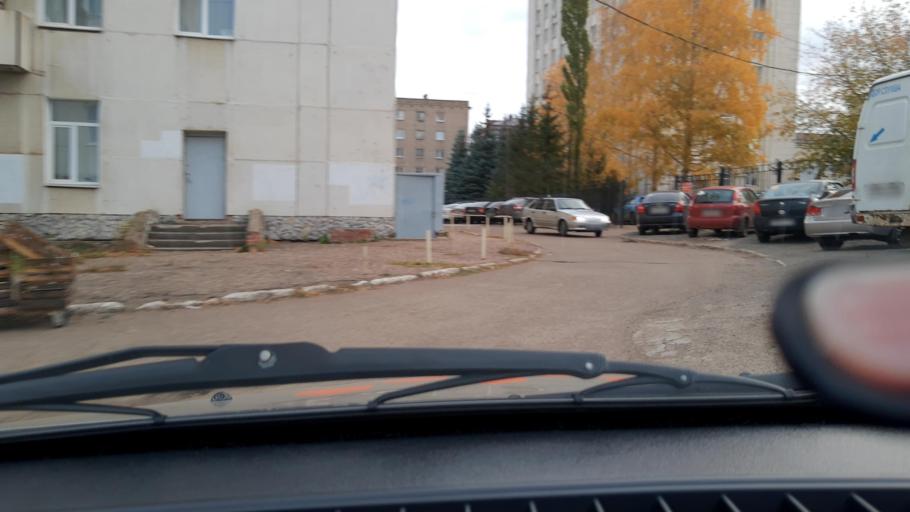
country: RU
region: Bashkortostan
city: Ufa
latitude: 54.7345
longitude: 55.9740
